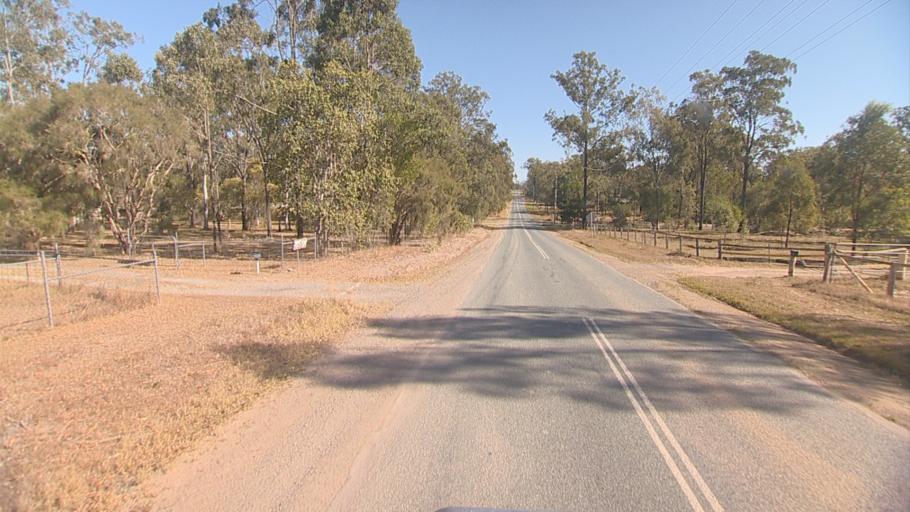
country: AU
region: Queensland
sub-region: Logan
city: Cedar Vale
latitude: -27.8497
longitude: 153.0363
